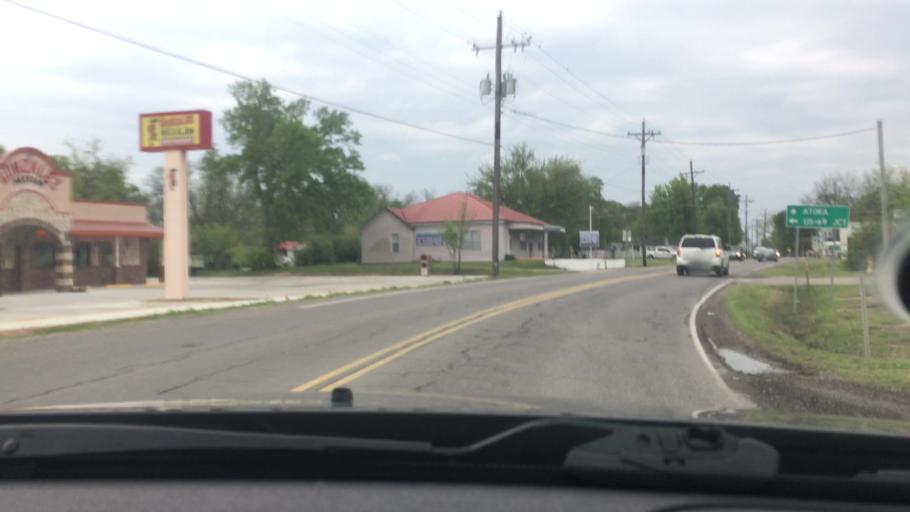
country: US
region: Oklahoma
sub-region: Coal County
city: Coalgate
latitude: 34.5354
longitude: -96.2165
